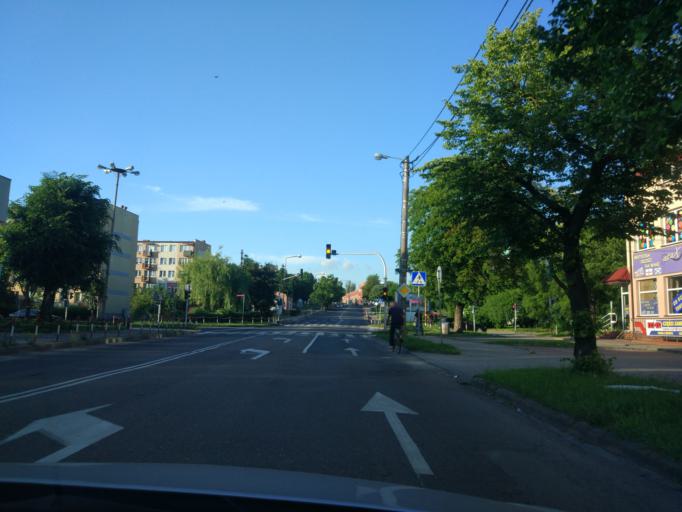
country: PL
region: Lodz Voivodeship
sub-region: Powiat kutnowski
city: Kutno
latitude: 52.2269
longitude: 19.3659
